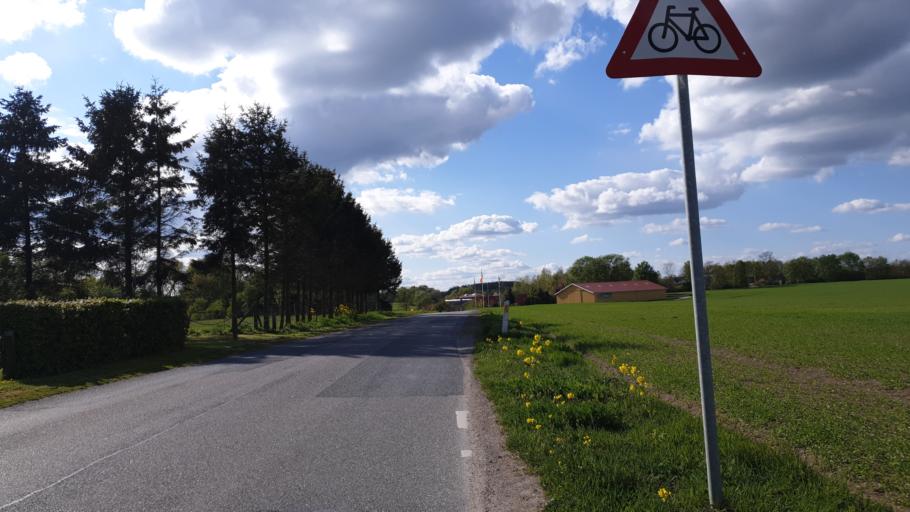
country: DK
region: Central Jutland
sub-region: Hedensted Kommune
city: Hedensted
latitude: 55.8093
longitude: 9.6741
